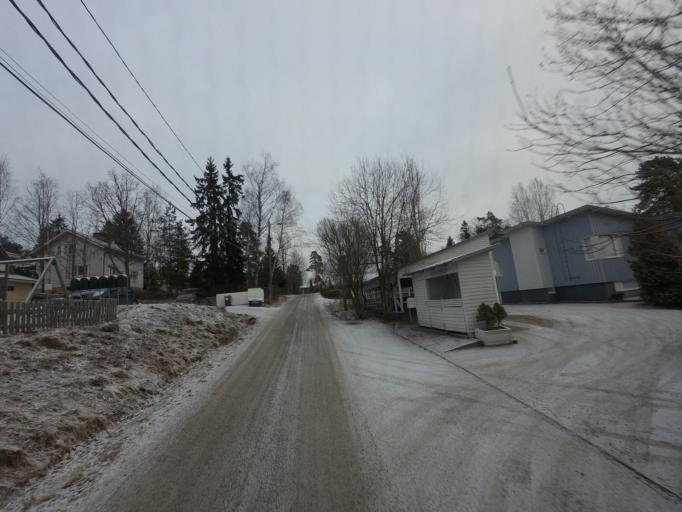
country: FI
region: Uusimaa
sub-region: Helsinki
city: Kauniainen
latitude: 60.2019
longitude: 24.6938
